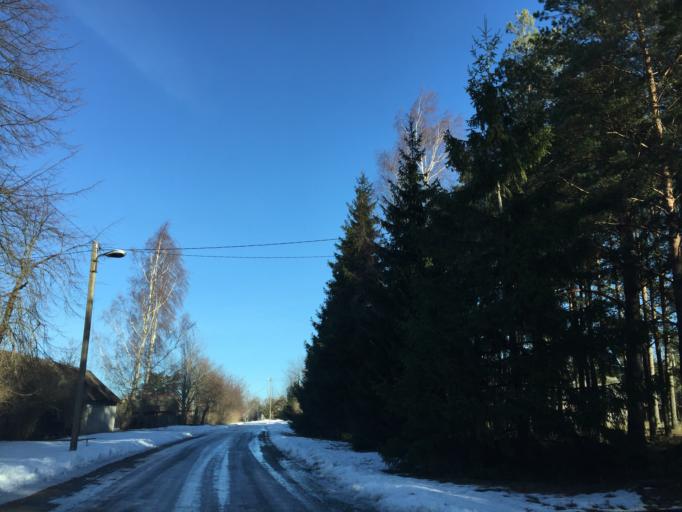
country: LV
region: Salacgrivas
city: Ainazi
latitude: 58.0832
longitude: 24.4892
